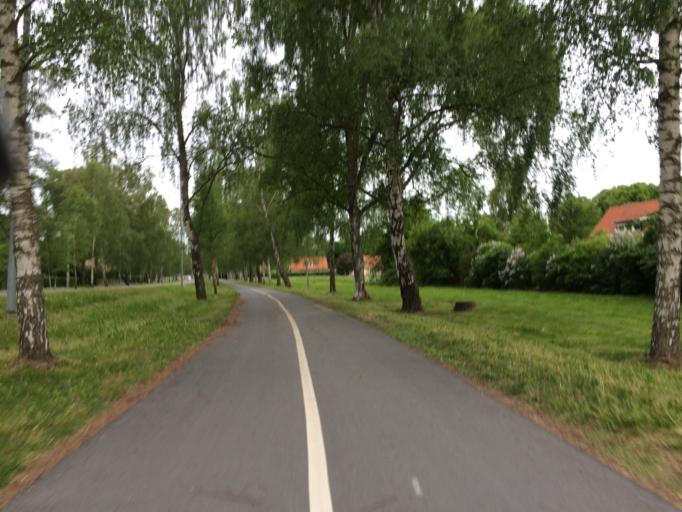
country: SE
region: Stockholm
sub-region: Danderyds Kommun
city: Djursholm
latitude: 59.3983
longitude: 18.0845
